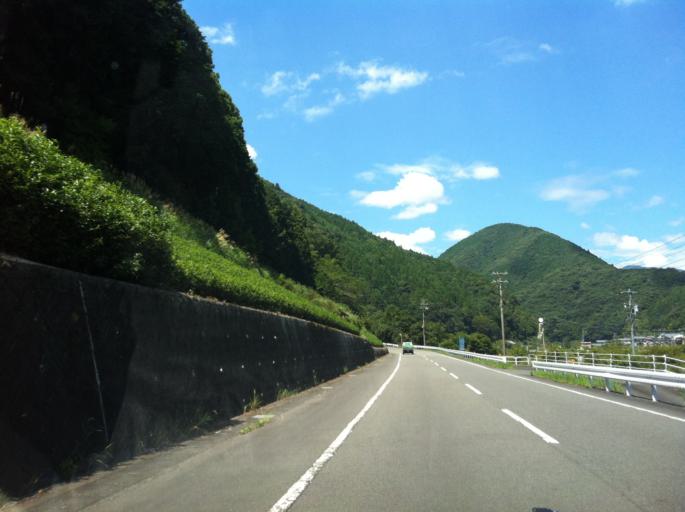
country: JP
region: Shizuoka
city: Shizuoka-shi
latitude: 35.0634
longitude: 138.2453
